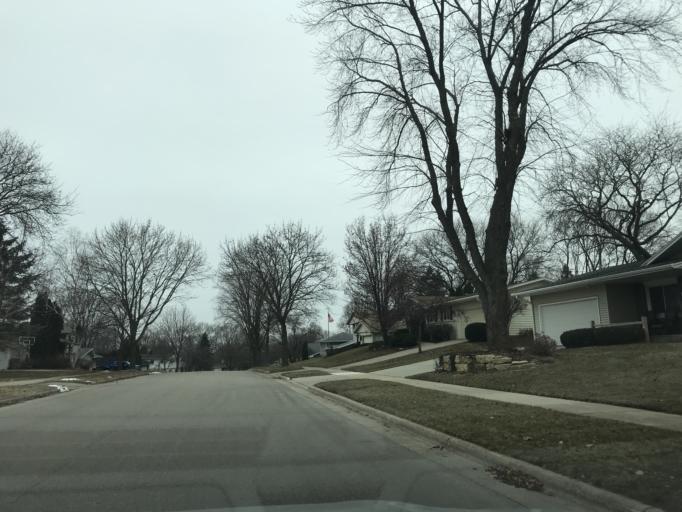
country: US
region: Wisconsin
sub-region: Dane County
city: Monona
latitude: 43.0869
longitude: -89.2909
